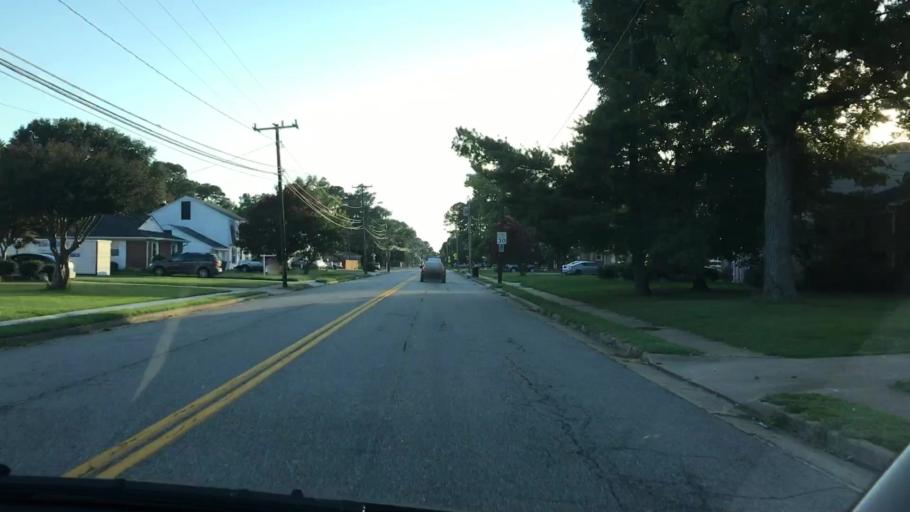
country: US
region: Virginia
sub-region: City of Hampton
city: Hampton
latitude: 37.0586
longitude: -76.3681
